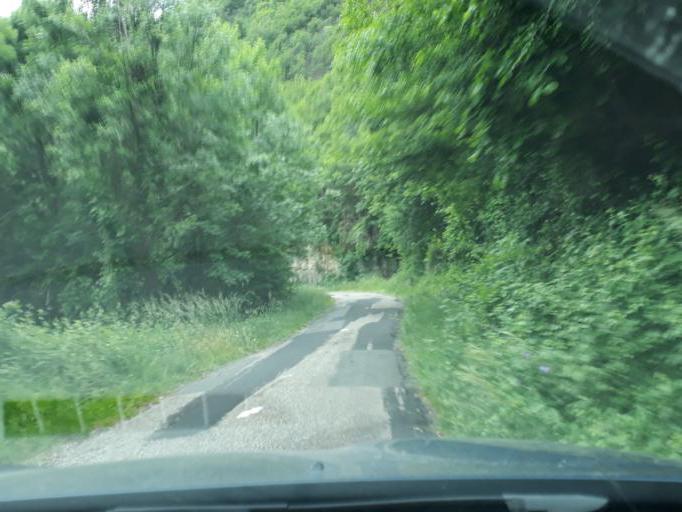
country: FR
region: Languedoc-Roussillon
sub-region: Departement de l'Herault
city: Lodeve
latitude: 43.7994
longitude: 3.2659
